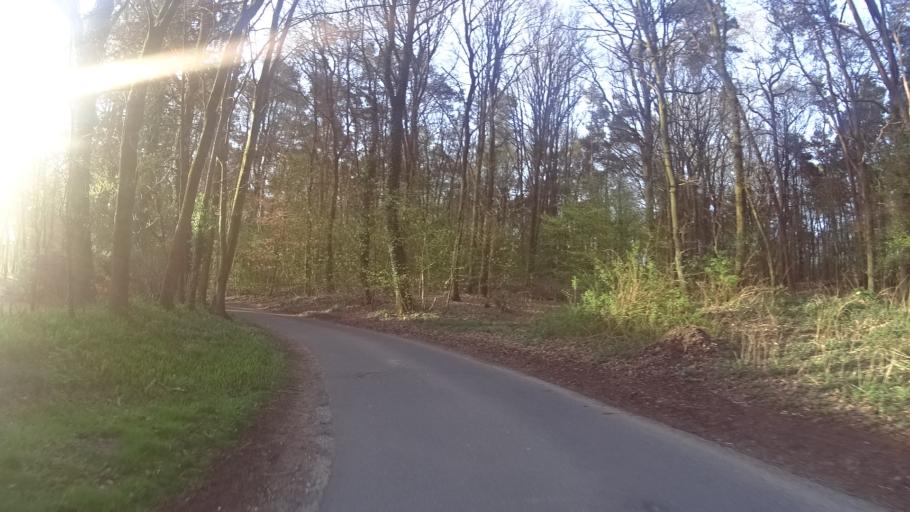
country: DE
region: North Rhine-Westphalia
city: Emsdetten
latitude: 52.2183
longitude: 7.5075
